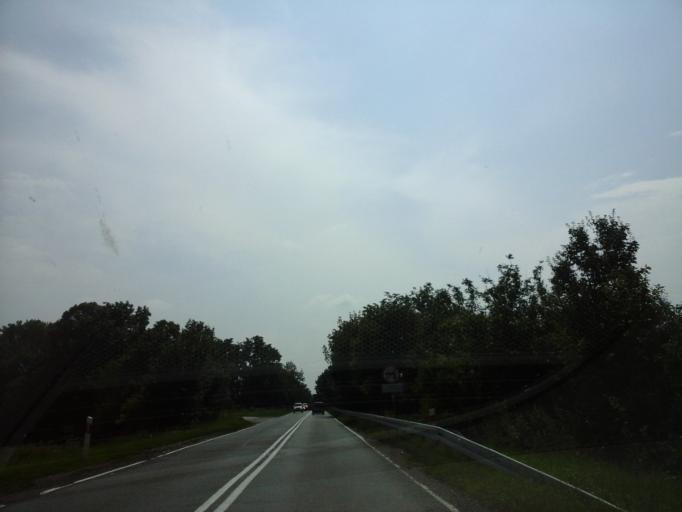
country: PL
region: Lower Silesian Voivodeship
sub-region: Powiat wroclawski
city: Zorawina
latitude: 50.9620
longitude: 17.0733
